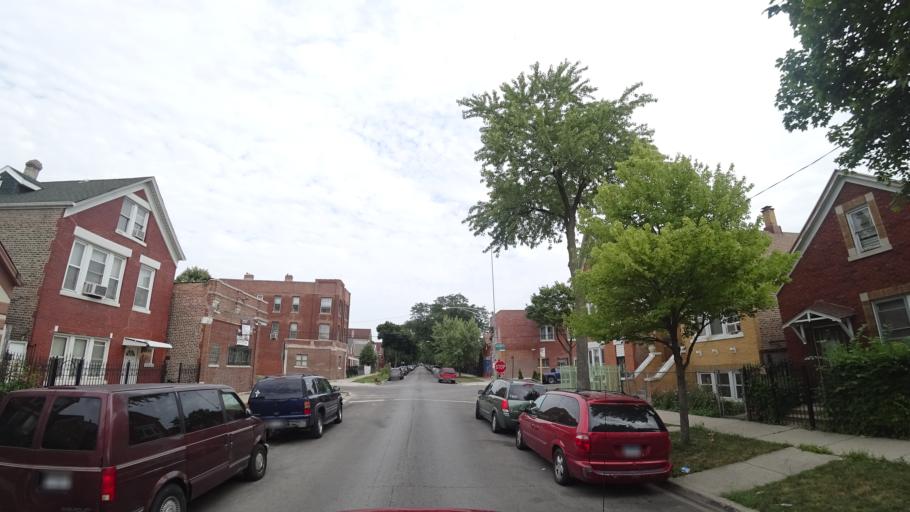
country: US
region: Illinois
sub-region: Cook County
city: Cicero
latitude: 41.8385
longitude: -87.7122
